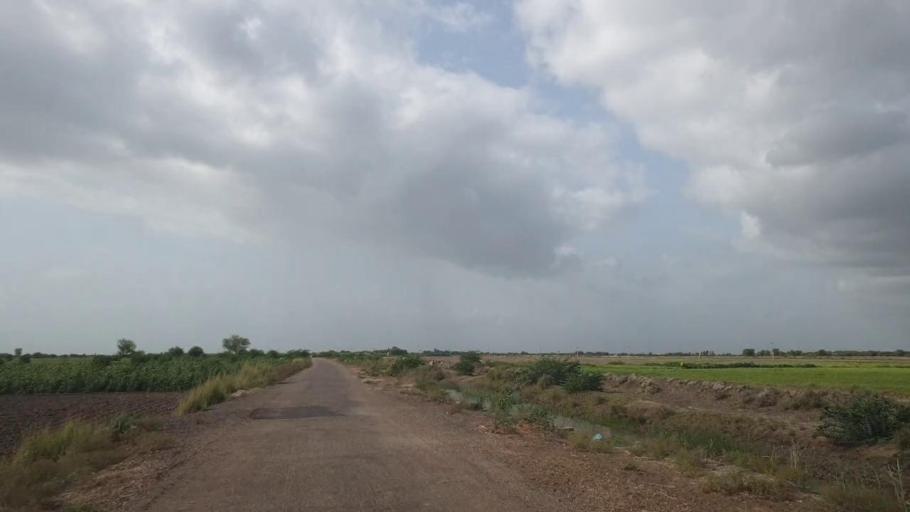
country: PK
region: Sindh
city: Kadhan
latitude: 24.5631
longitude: 69.0639
